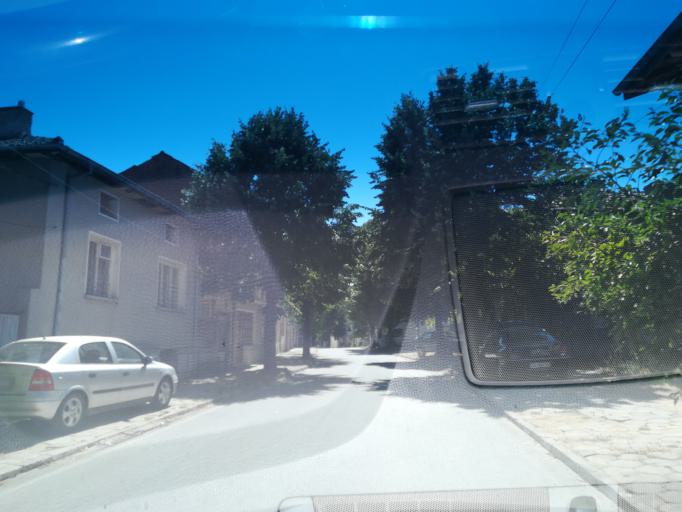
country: BG
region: Pazardzhik
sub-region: Obshtina Strelcha
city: Strelcha
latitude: 42.5087
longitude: 24.3203
